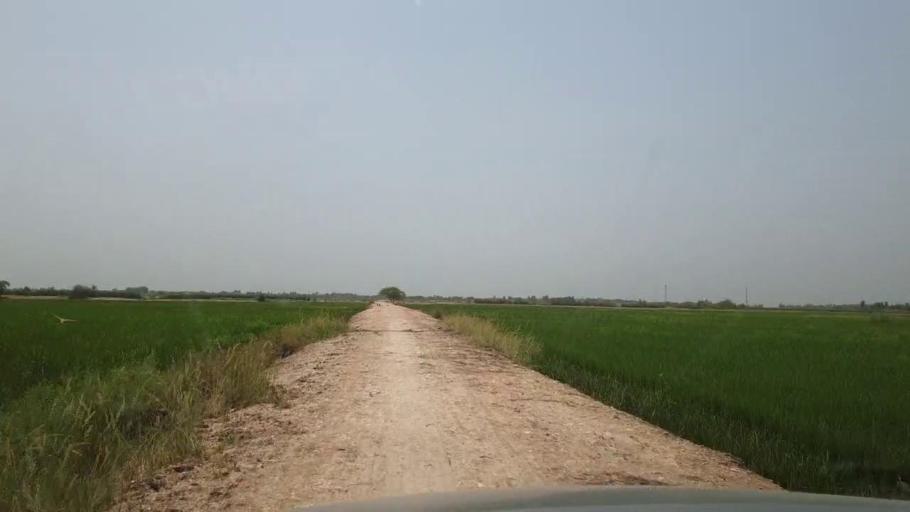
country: PK
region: Sindh
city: Garhi Yasin
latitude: 27.8620
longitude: 68.4808
